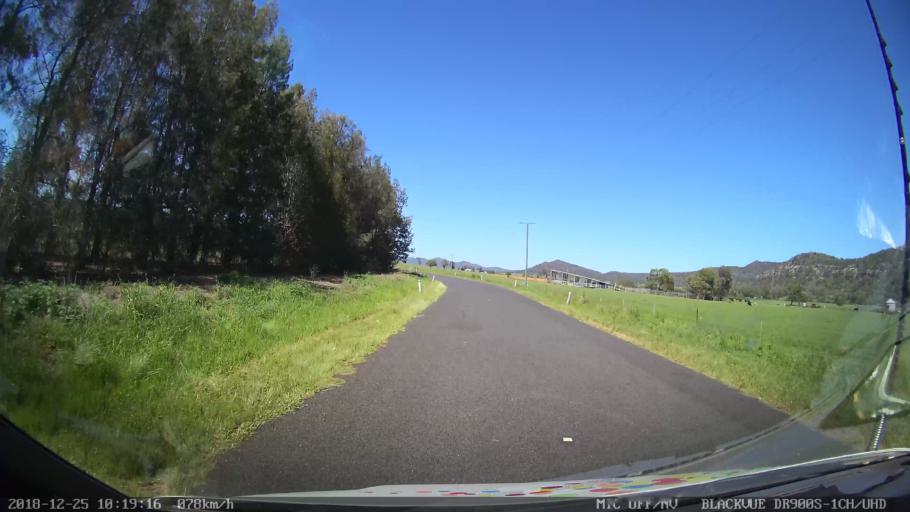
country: AU
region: New South Wales
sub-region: Muswellbrook
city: Denman
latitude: -32.3492
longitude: 150.5599
